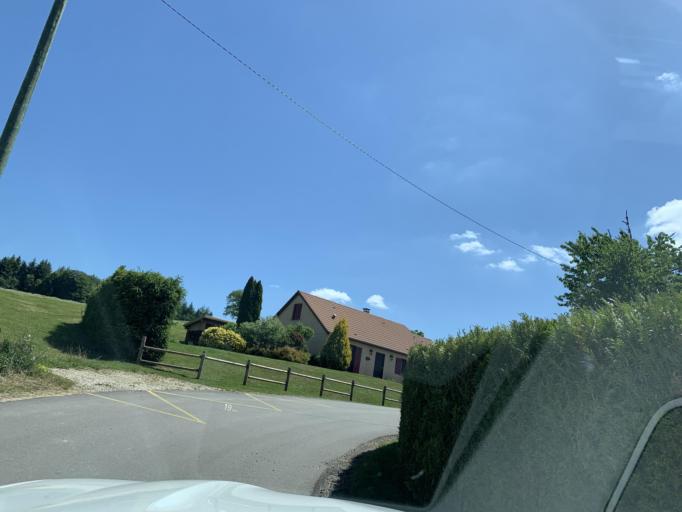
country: FR
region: Lorraine
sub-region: Departement des Vosges
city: Uzemain
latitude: 48.1377
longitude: 6.3336
